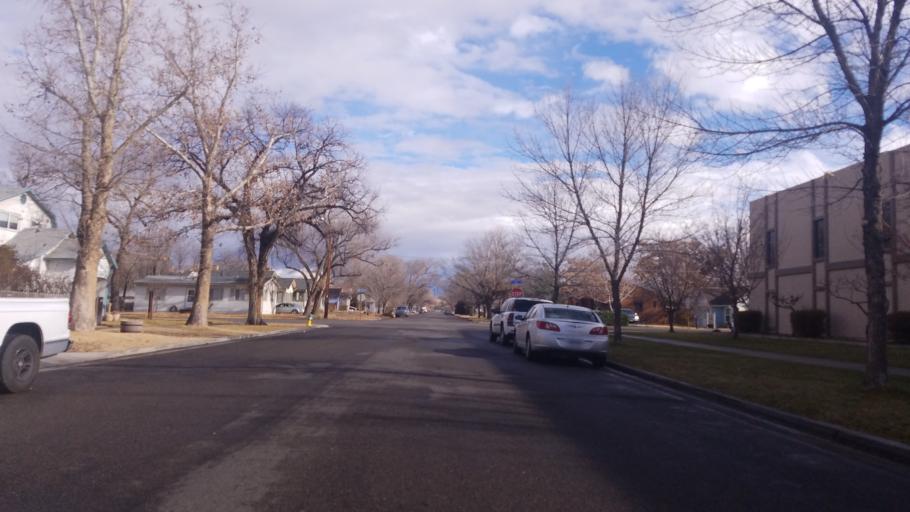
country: US
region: Colorado
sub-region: Mesa County
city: Grand Junction
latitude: 39.0663
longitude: -108.5531
